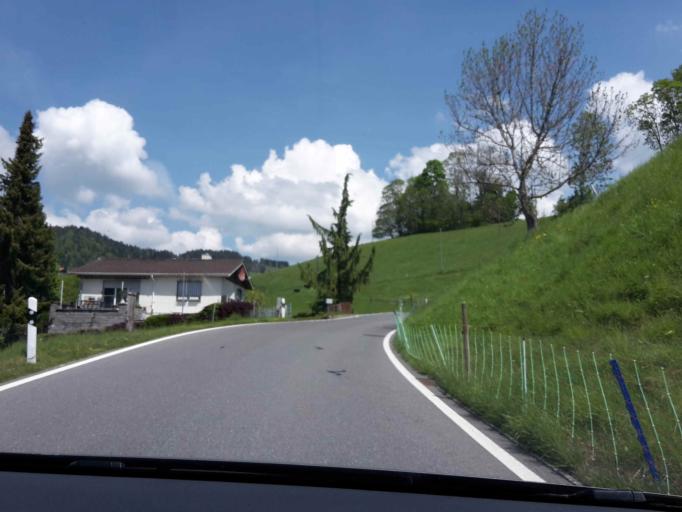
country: CH
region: Bern
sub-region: Thun District
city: Hilterfingen
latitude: 46.7541
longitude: 7.6664
